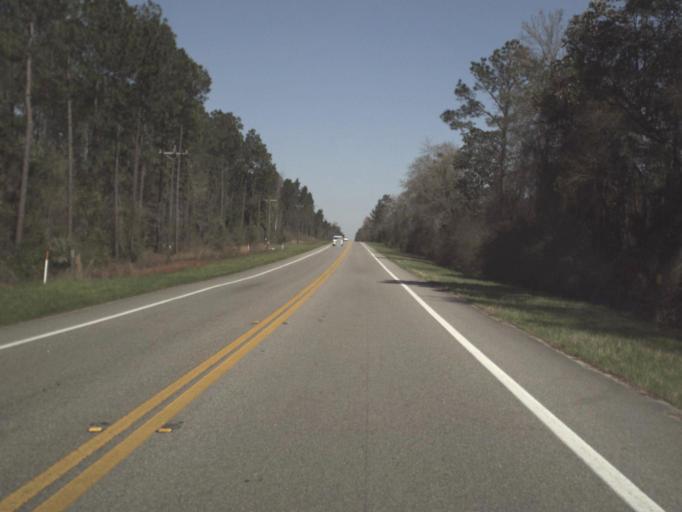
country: US
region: Florida
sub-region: Gadsden County
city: Gretna
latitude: 30.3840
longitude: -84.7250
